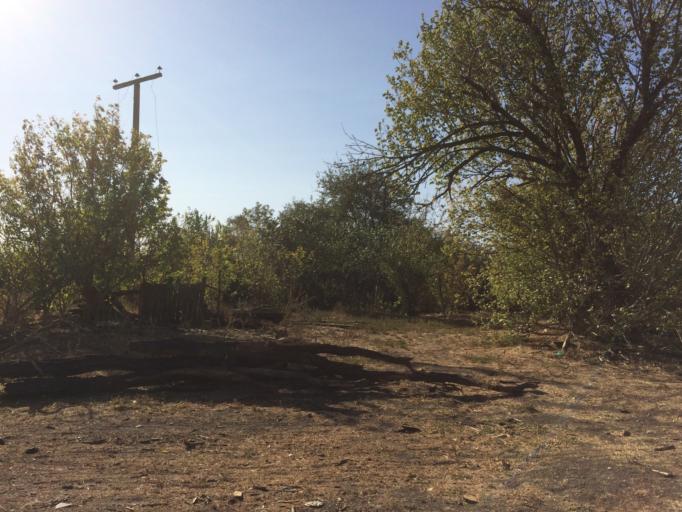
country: RU
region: Rostov
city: Gigant
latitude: 46.5139
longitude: 41.1875
